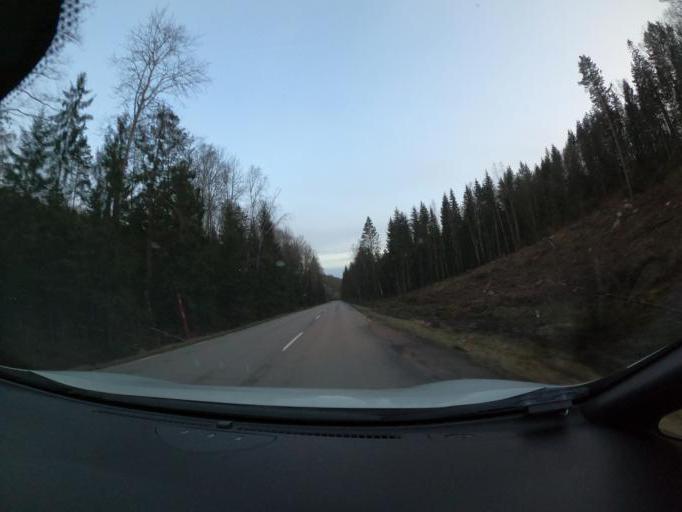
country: SE
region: Vaestra Goetaland
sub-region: Harryda Kommun
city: Landvetter
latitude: 57.6291
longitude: 12.1801
